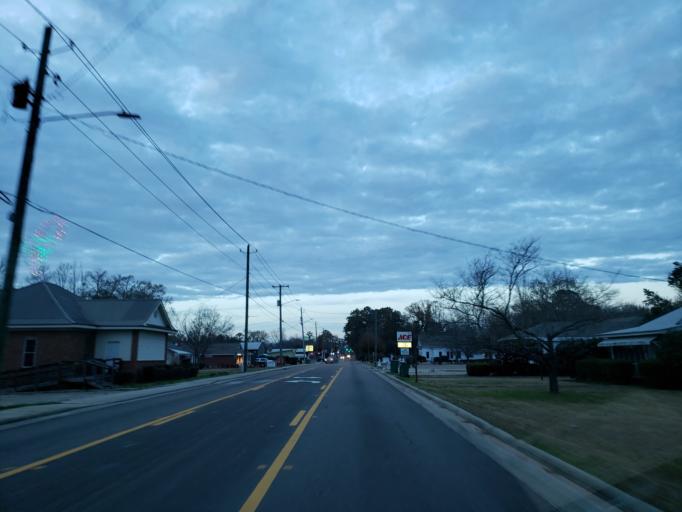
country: US
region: Mississippi
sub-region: Forrest County
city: Petal
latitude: 31.3409
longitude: -89.2629
